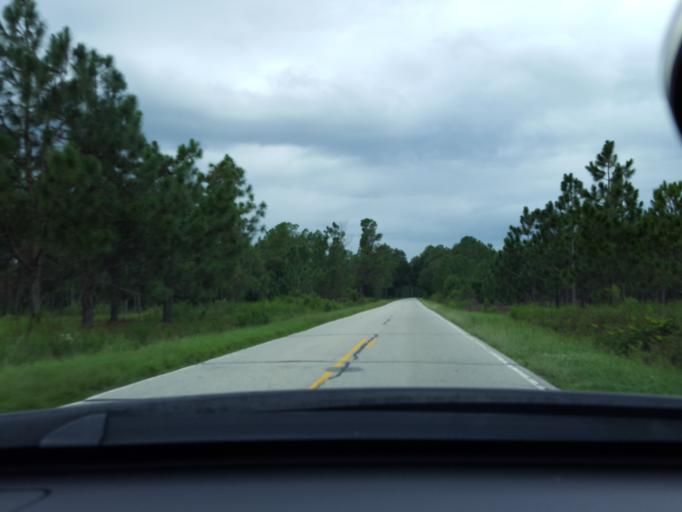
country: US
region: North Carolina
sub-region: Sampson County
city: Clinton
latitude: 34.8001
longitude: -78.2672
